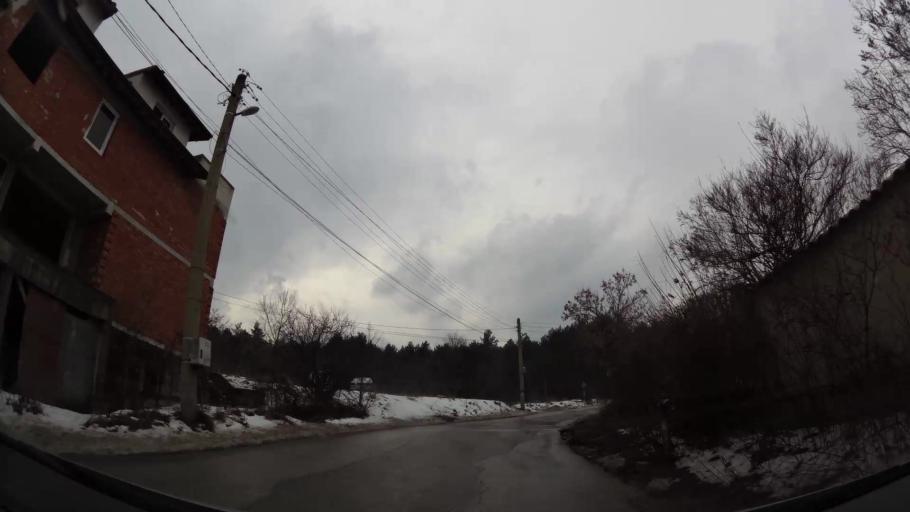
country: BG
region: Sofiya
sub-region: Obshtina Bozhurishte
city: Bozhurishte
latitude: 42.6745
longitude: 23.2239
